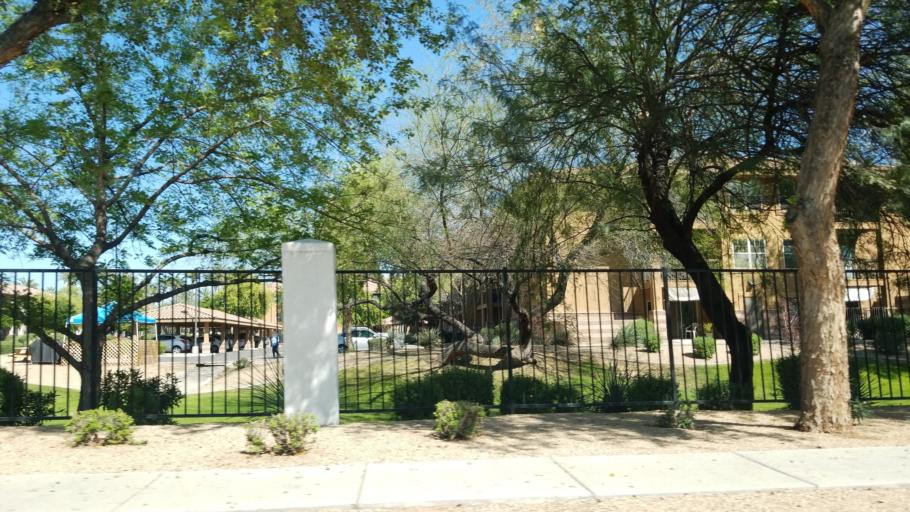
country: US
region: Arizona
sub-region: Maricopa County
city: Glendale
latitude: 33.5521
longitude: -112.1731
